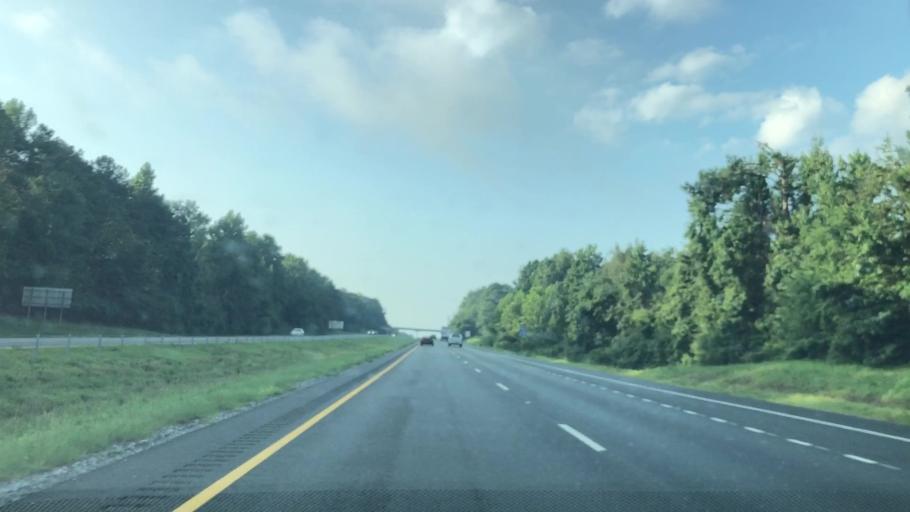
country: US
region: Alabama
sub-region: Chilton County
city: Clanton
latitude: 32.8382
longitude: -86.5935
